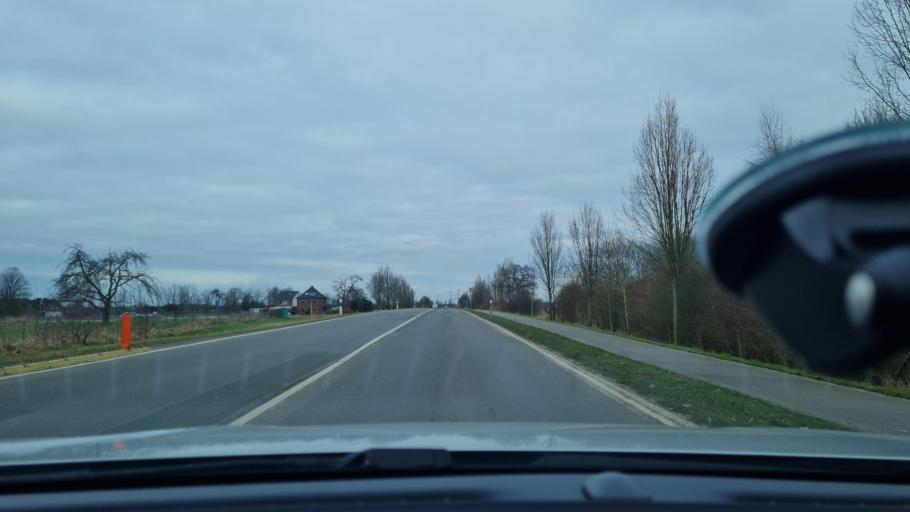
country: DE
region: North Rhine-Westphalia
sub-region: Regierungsbezirk Dusseldorf
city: Voerde
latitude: 51.6017
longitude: 6.6615
